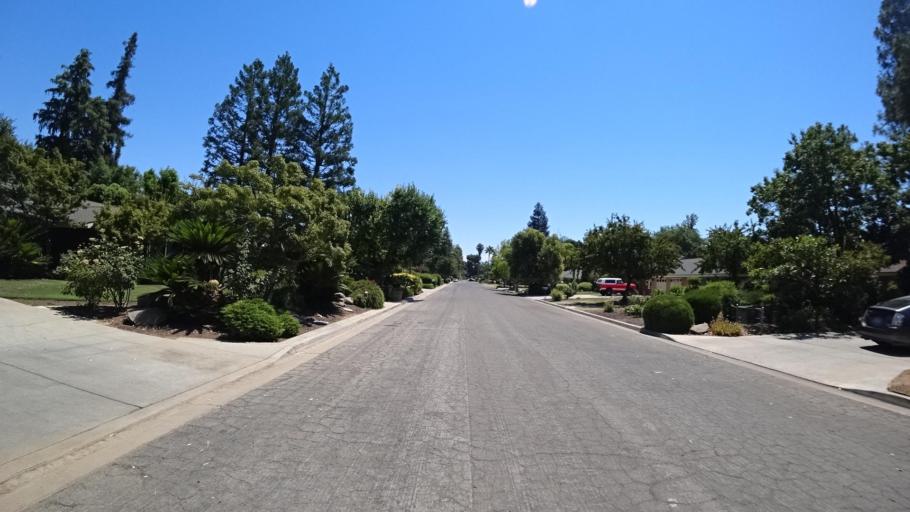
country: US
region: California
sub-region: Fresno County
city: Sunnyside
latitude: 36.7277
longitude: -119.7258
